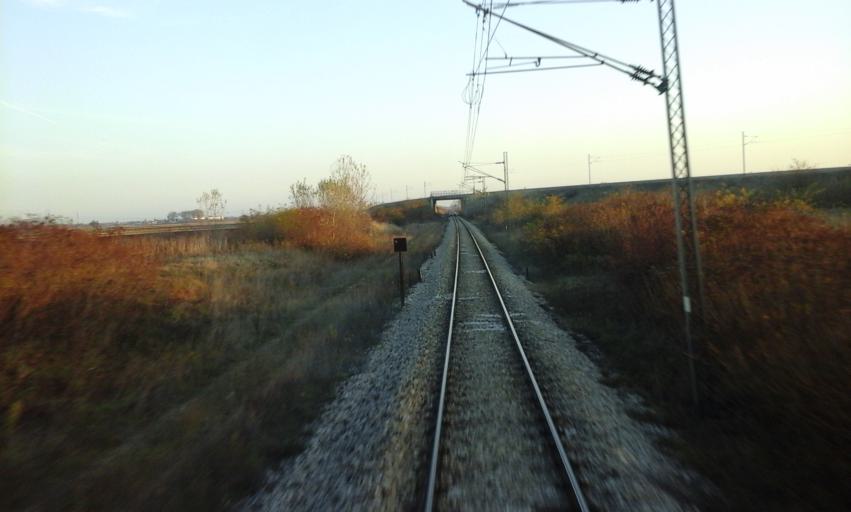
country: RS
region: Autonomna Pokrajina Vojvodina
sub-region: Sremski Okrug
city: Ingija
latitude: 45.0185
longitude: 20.1142
